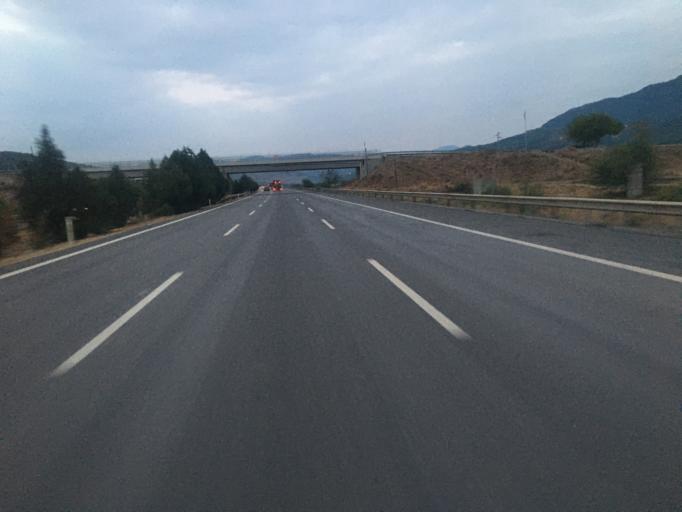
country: TR
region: Osmaniye
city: Osmaniye
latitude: 37.1467
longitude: 36.3359
